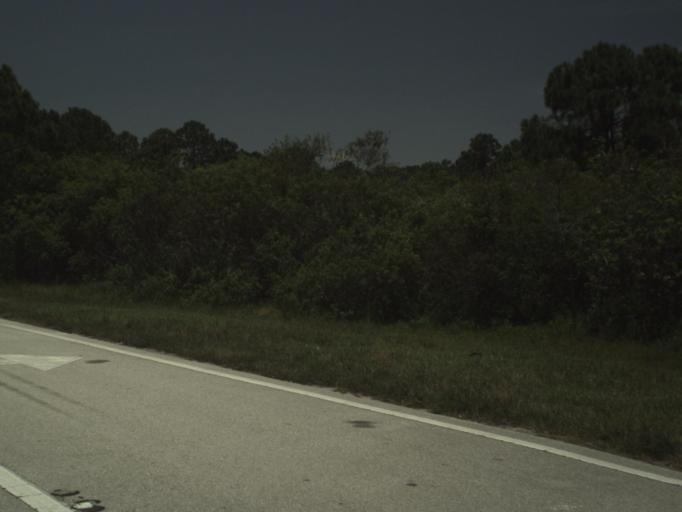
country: US
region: Florida
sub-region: Martin County
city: Palm City
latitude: 27.1620
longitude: -80.3825
